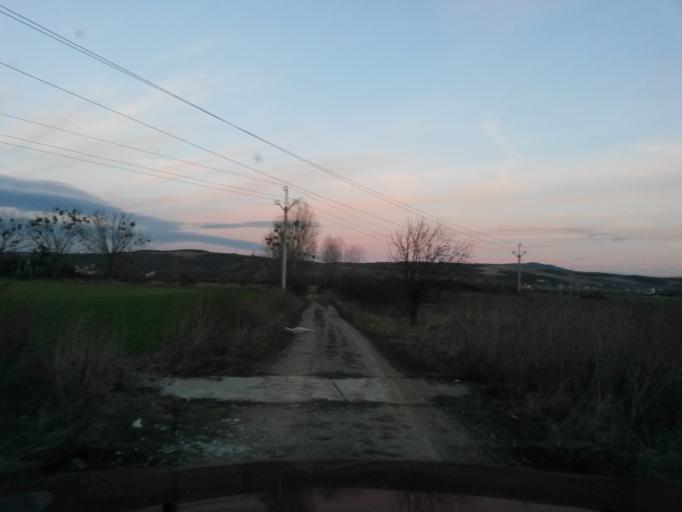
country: SK
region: Kosicky
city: Kosice
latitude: 48.7038
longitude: 21.3263
